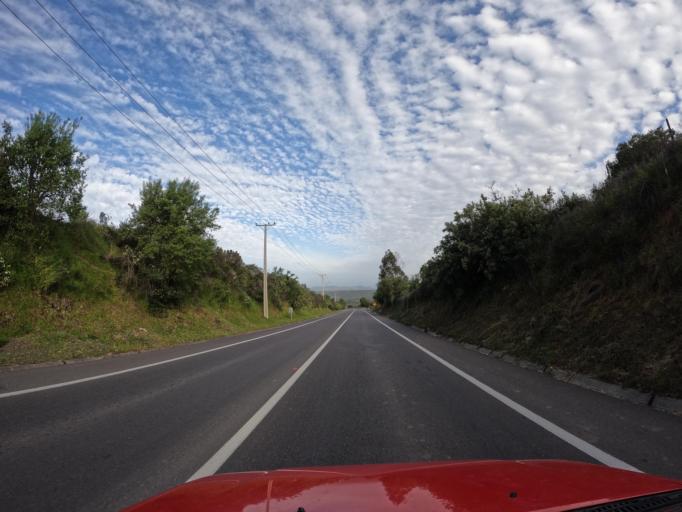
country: CL
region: Valparaiso
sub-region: San Antonio Province
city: San Antonio
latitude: -34.0494
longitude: -71.6072
